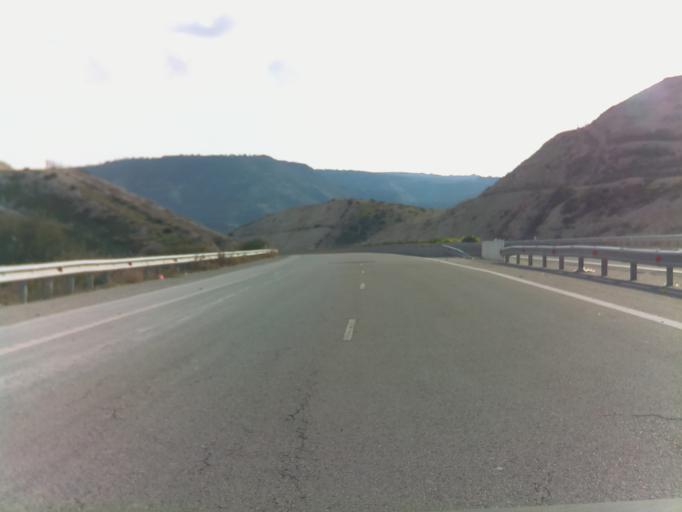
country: CY
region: Limassol
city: Pissouri
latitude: 34.6675
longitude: 32.6441
